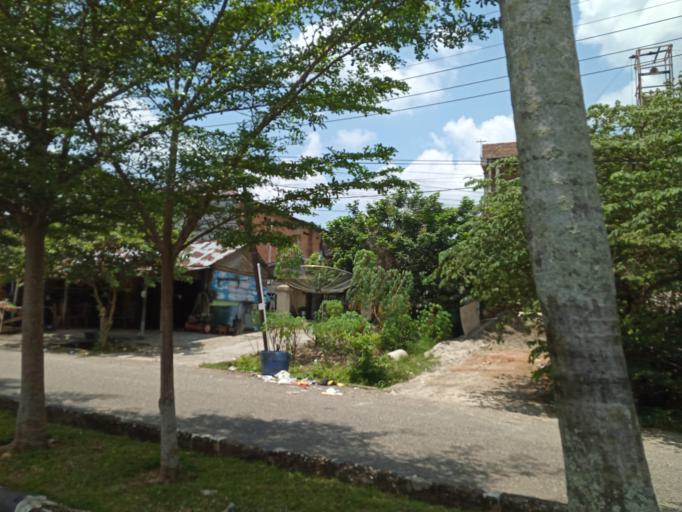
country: ID
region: Jambi
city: Bangko
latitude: -2.0535
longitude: 102.2820
